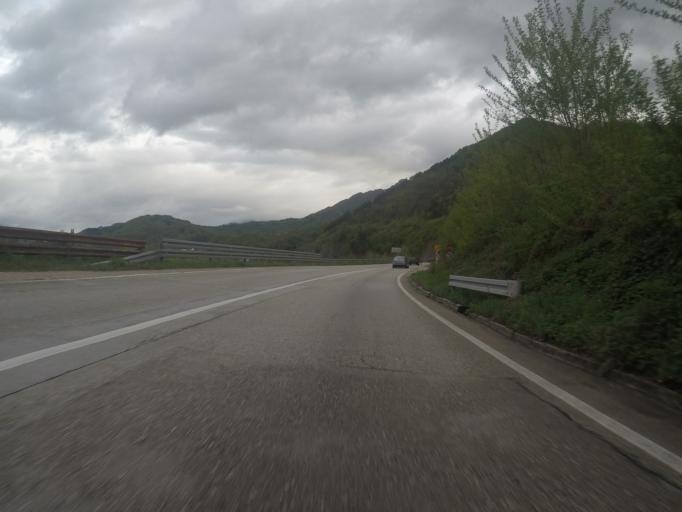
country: BA
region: Federation of Bosnia and Herzegovina
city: Konjic
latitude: 43.6809
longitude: 17.9050
